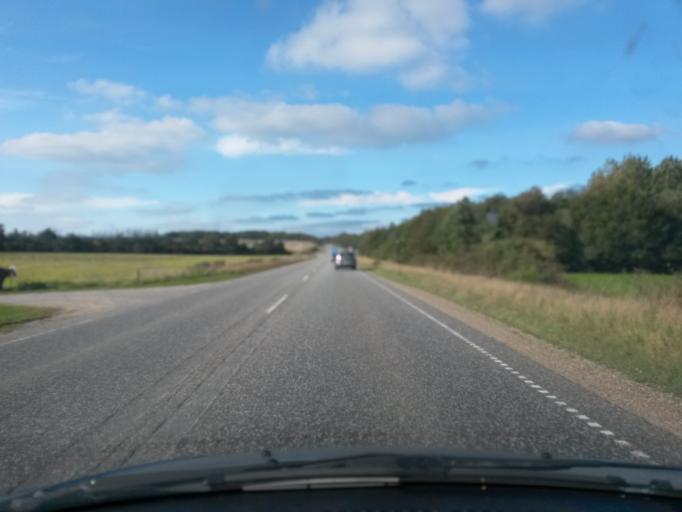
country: DK
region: Central Jutland
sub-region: Herning Kommune
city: Avlum
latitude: 56.2794
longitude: 8.7542
